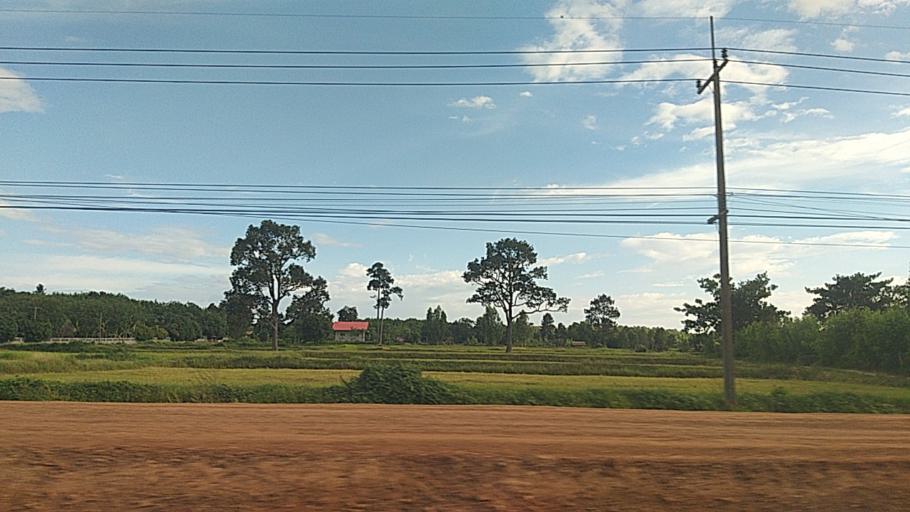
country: TH
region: Surin
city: Kap Choeng
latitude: 14.4648
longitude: 103.6418
